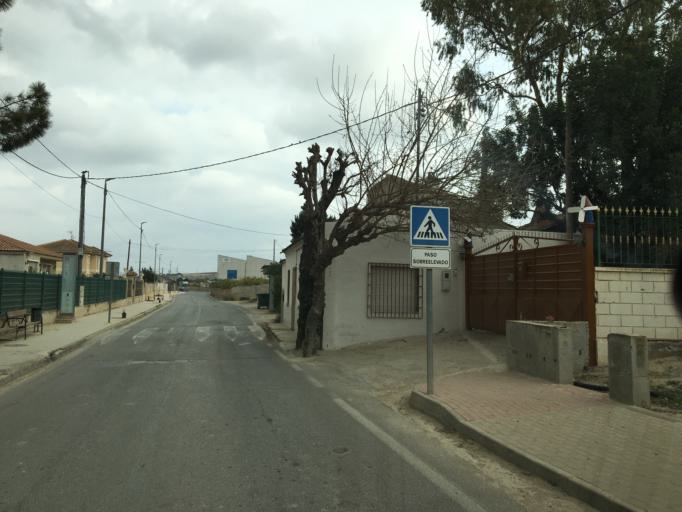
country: ES
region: Murcia
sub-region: Murcia
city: Beniel
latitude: 38.0168
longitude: -0.9868
